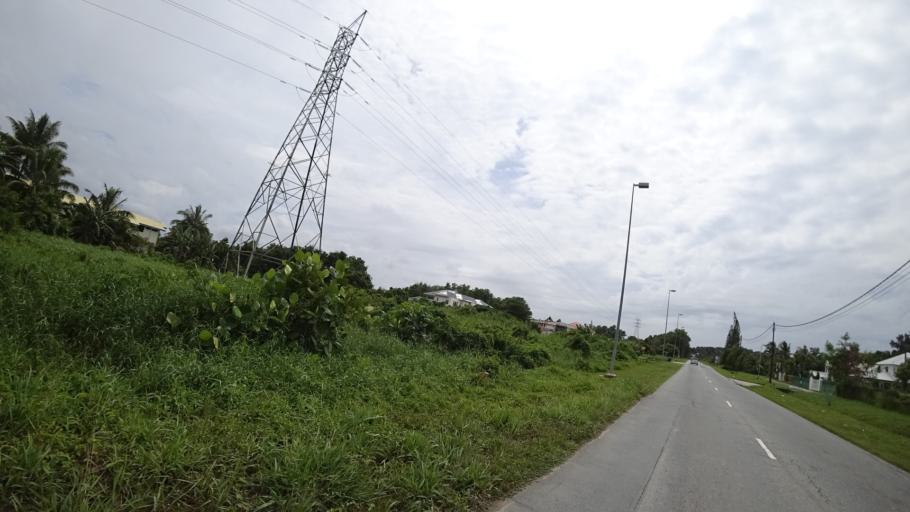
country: BN
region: Tutong
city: Tutong
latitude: 4.8176
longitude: 114.7100
